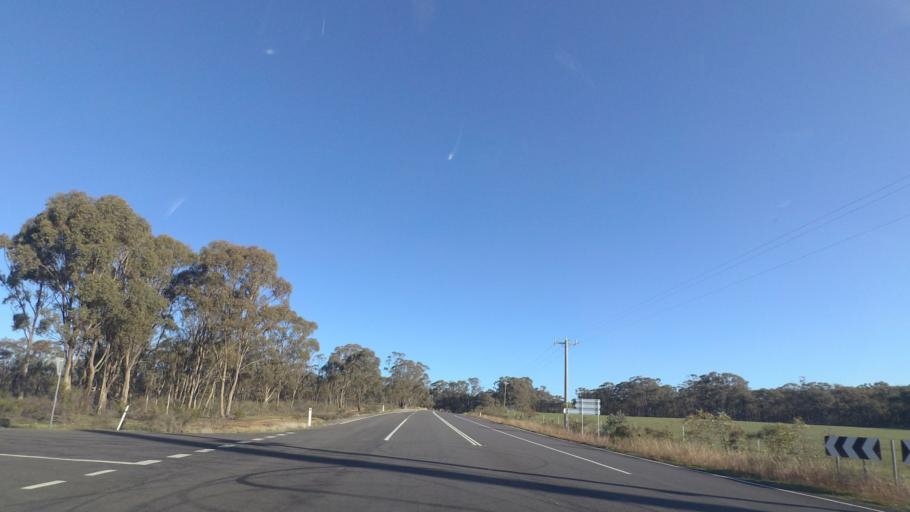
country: AU
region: Victoria
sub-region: Greater Bendigo
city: Kennington
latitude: -36.8717
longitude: 144.4987
